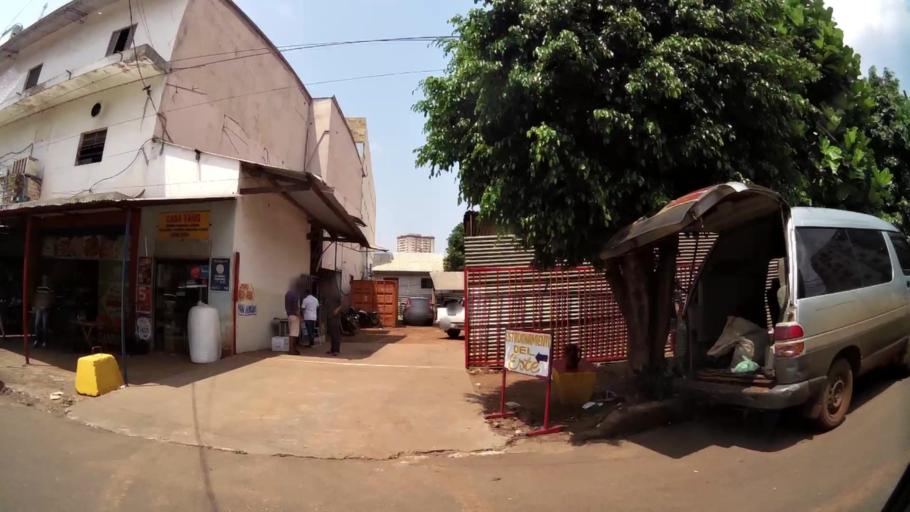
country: PY
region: Alto Parana
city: Ciudad del Este
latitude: -25.5126
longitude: -54.6113
